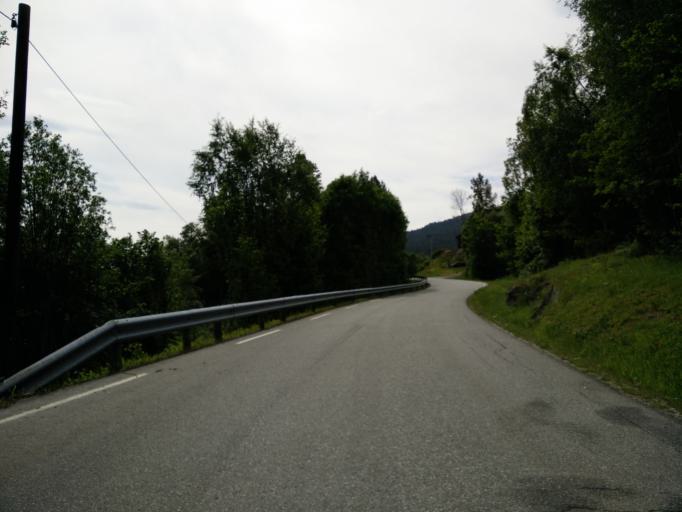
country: NO
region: More og Romsdal
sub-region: Kristiansund
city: Rensvik
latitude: 63.0243
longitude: 7.9528
